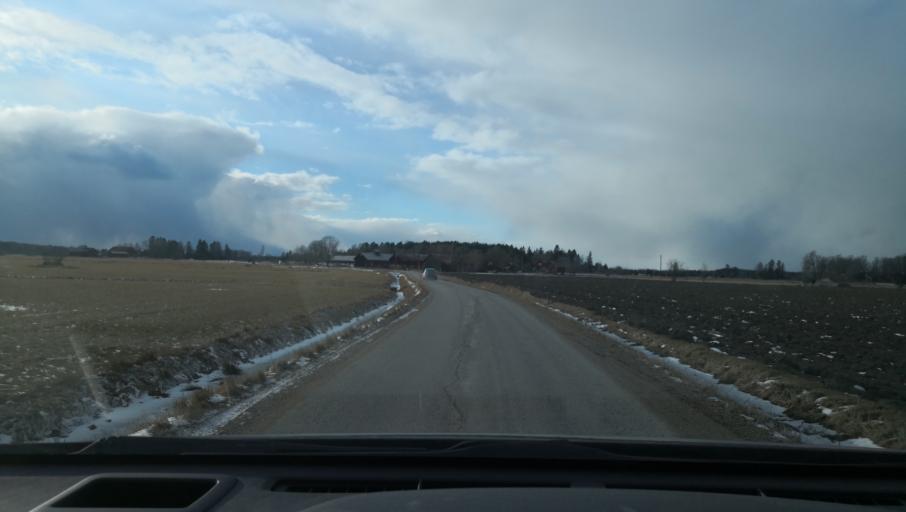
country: SE
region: Uppsala
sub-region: Enkopings Kommun
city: Irsta
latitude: 59.6956
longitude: 16.9713
